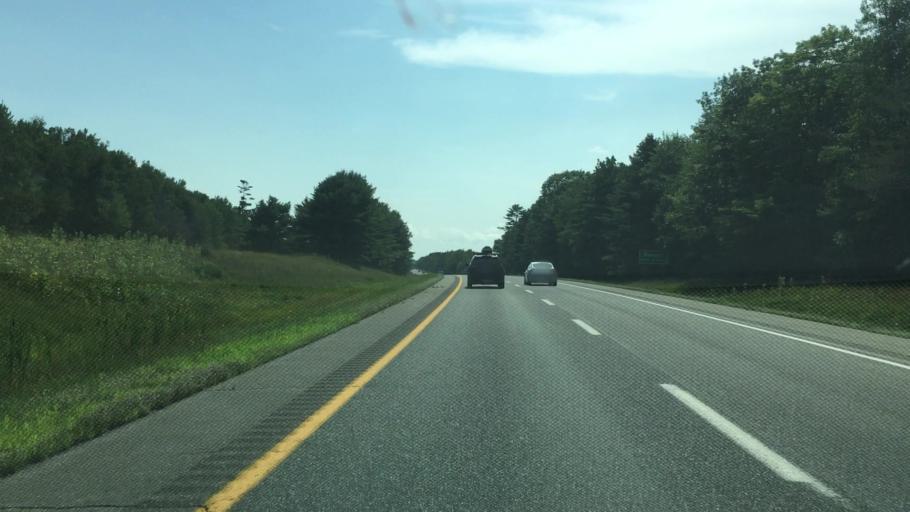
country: US
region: Maine
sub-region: Penobscot County
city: Veazie
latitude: 44.8574
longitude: -68.7216
